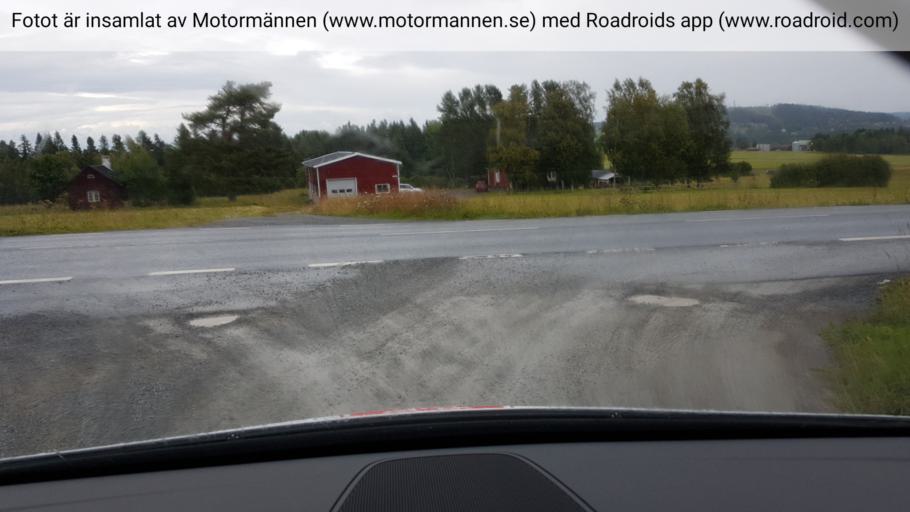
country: SE
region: Jaemtland
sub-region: OEstersunds Kommun
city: Ostersund
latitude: 63.1745
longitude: 14.5324
